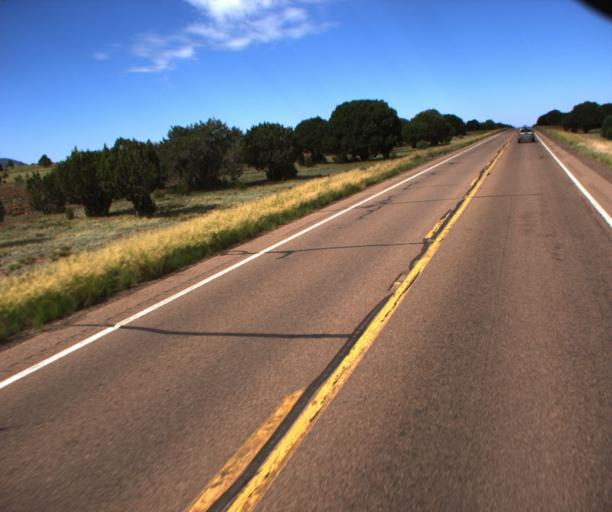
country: US
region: Arizona
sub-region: Navajo County
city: White Mountain Lake
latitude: 34.2766
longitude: -109.8907
